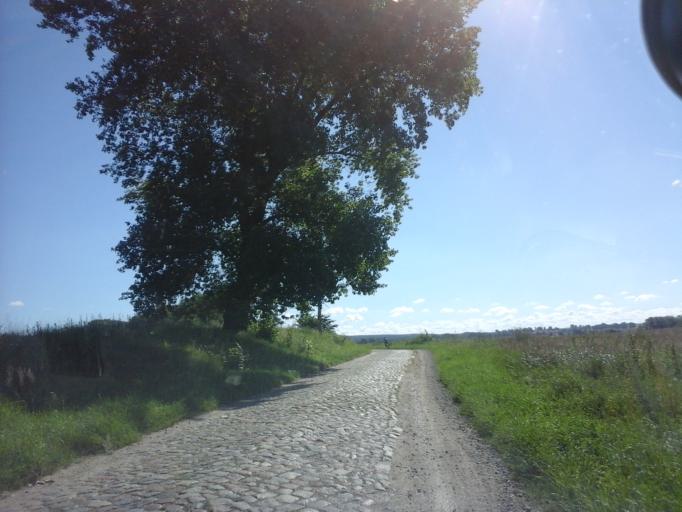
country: PL
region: West Pomeranian Voivodeship
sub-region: Powiat choszczenski
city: Choszczno
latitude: 53.1824
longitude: 15.4530
